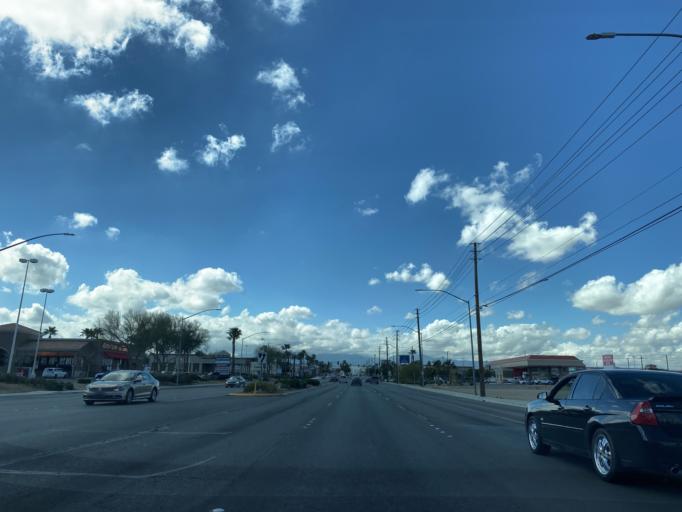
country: US
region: Nevada
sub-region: Clark County
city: North Las Vegas
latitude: 36.2395
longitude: -115.1684
